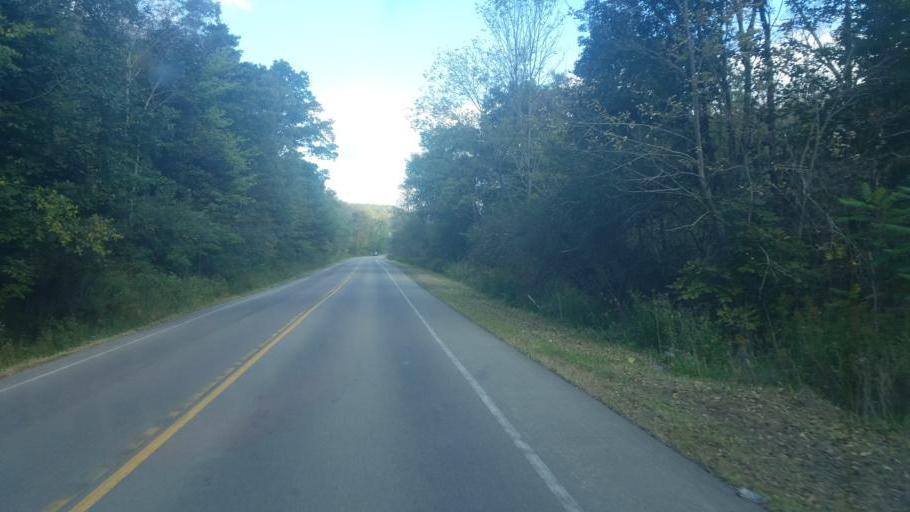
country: US
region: New York
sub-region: Allegany County
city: Cuba
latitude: 42.2279
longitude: -78.3116
